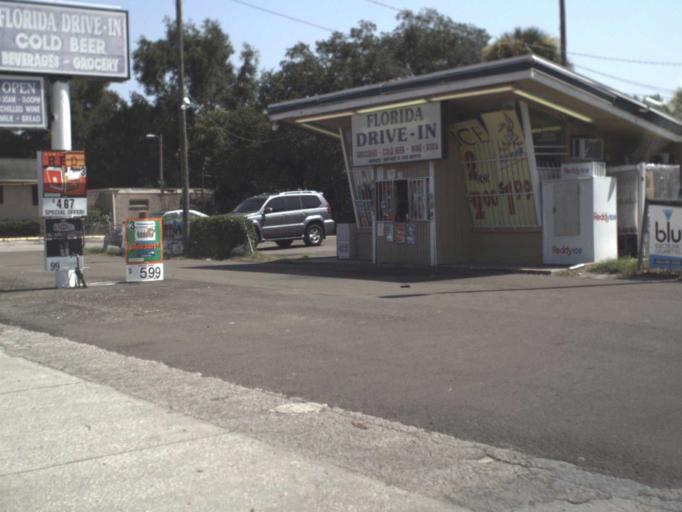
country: US
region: Florida
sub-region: Hillsborough County
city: Egypt Lake-Leto
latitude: 28.0071
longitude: -82.4594
